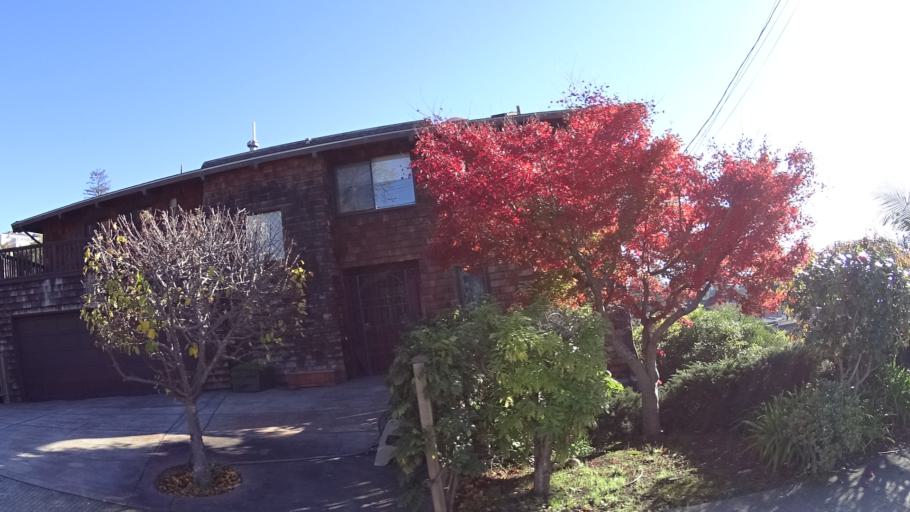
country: US
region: California
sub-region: Alameda County
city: Piedmont
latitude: 37.8272
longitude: -122.2276
